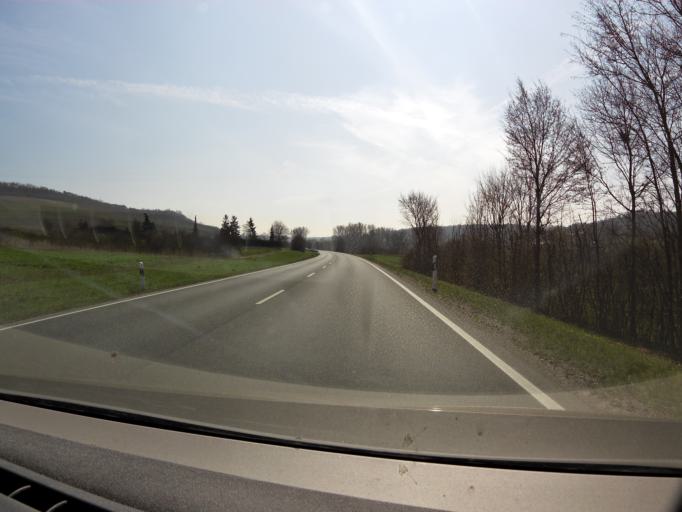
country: DE
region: Bavaria
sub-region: Regierungsbezirk Unterfranken
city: Sommerhausen
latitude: 49.6912
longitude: 10.0251
